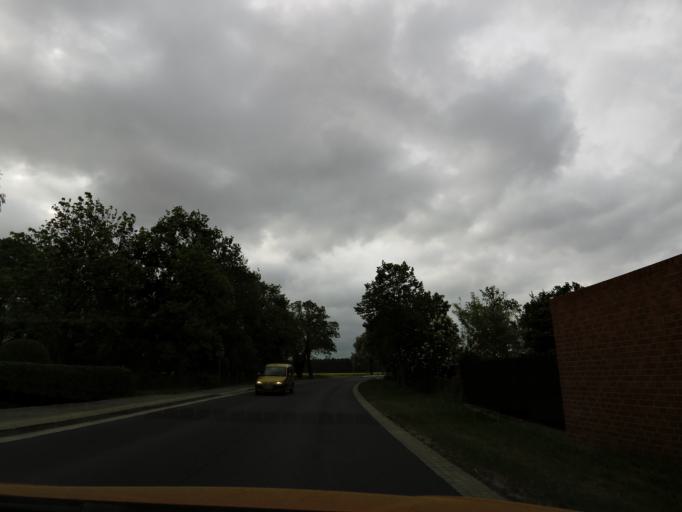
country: DE
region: Brandenburg
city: Treuenbrietzen
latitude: 52.1569
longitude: 12.9264
